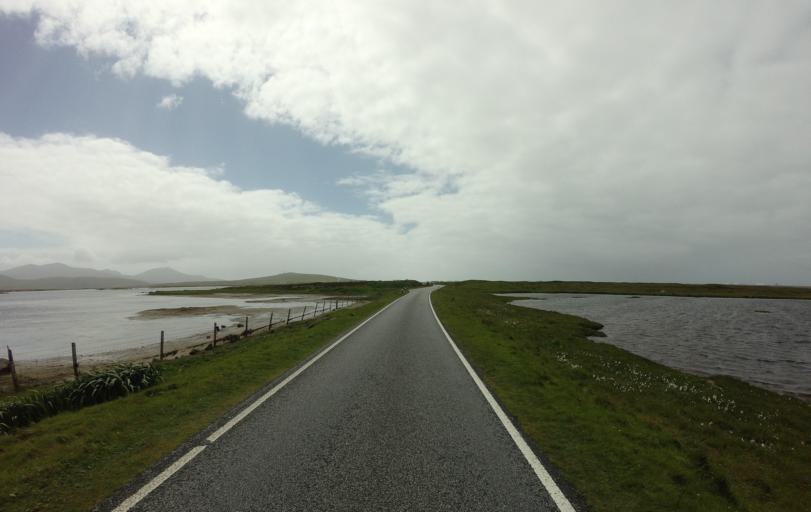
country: GB
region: Scotland
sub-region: Eilean Siar
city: Benbecula
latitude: 57.3655
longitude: -7.3525
